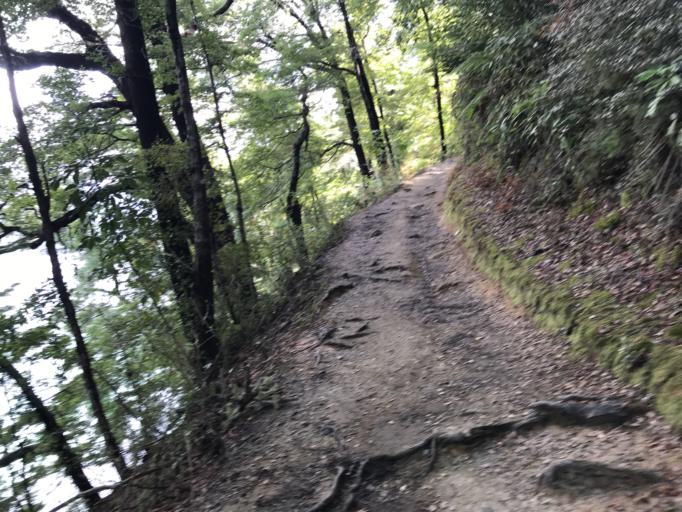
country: NZ
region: Marlborough
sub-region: Marlborough District
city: Picton
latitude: -41.2607
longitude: 173.9314
